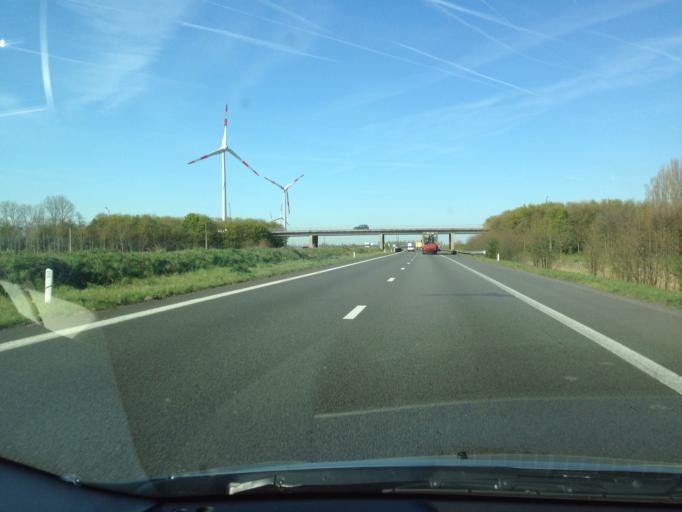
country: BE
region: Flanders
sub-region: Provincie West-Vlaanderen
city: Gistel
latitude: 51.1689
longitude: 2.9688
